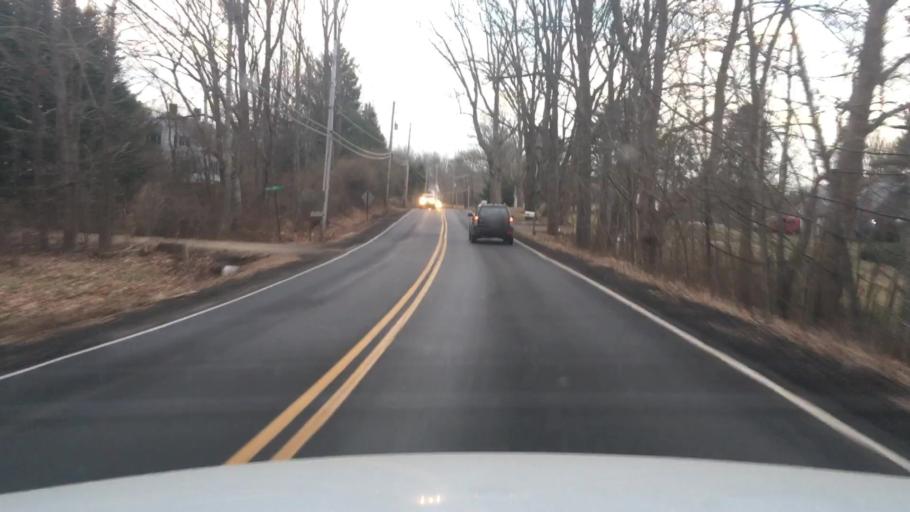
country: US
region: Maine
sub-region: Lincoln County
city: Damariscotta
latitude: 44.0088
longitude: -69.5311
